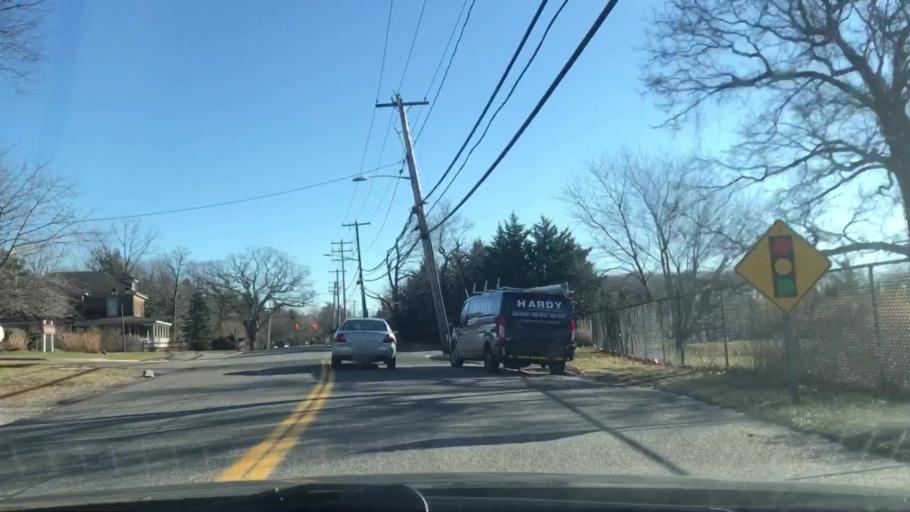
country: US
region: New York
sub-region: Suffolk County
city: Riverhead
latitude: 40.9373
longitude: -72.6740
